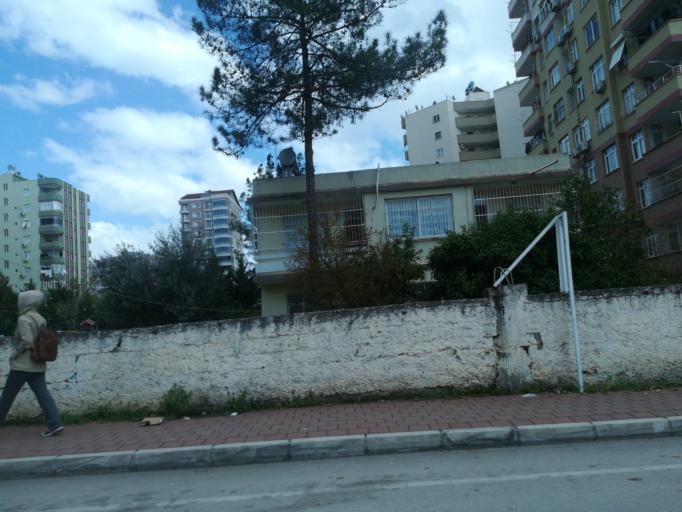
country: TR
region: Adana
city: Adana
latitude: 37.0357
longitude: 35.3126
